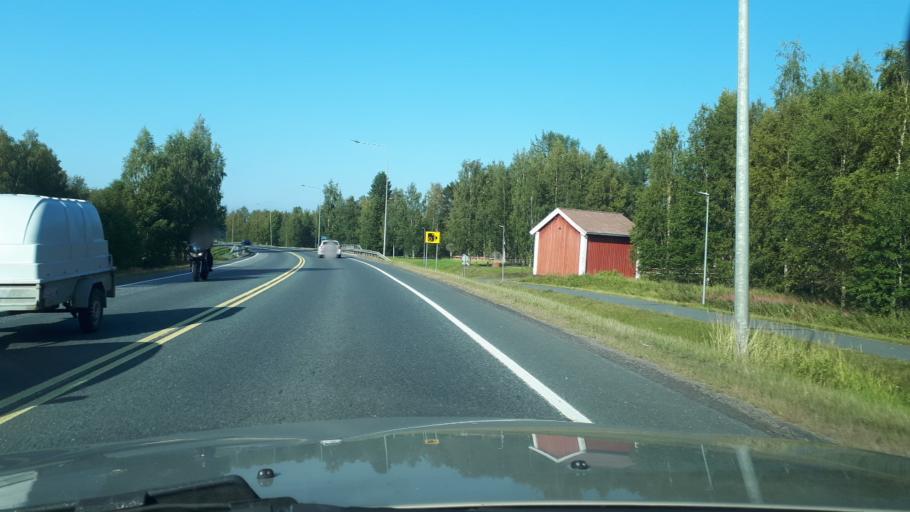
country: FI
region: Northern Ostrobothnia
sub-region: Oulunkaari
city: Ii
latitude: 65.3238
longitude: 25.3800
